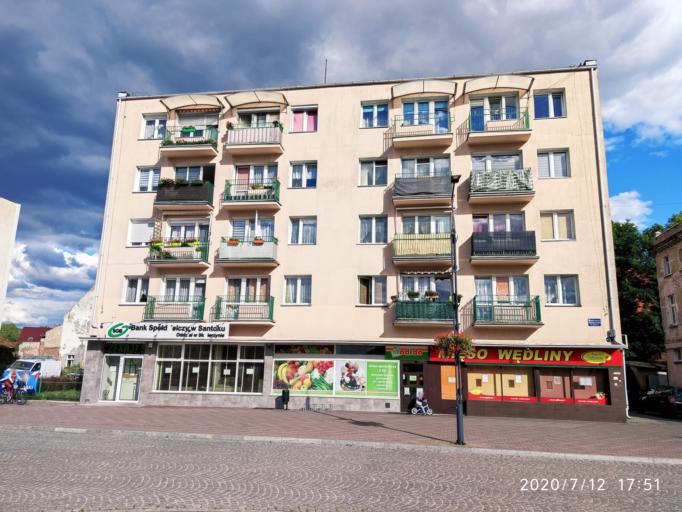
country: PL
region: Lubusz
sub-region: Powiat miedzyrzecki
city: Skwierzyna
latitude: 52.6000
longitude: 15.5022
